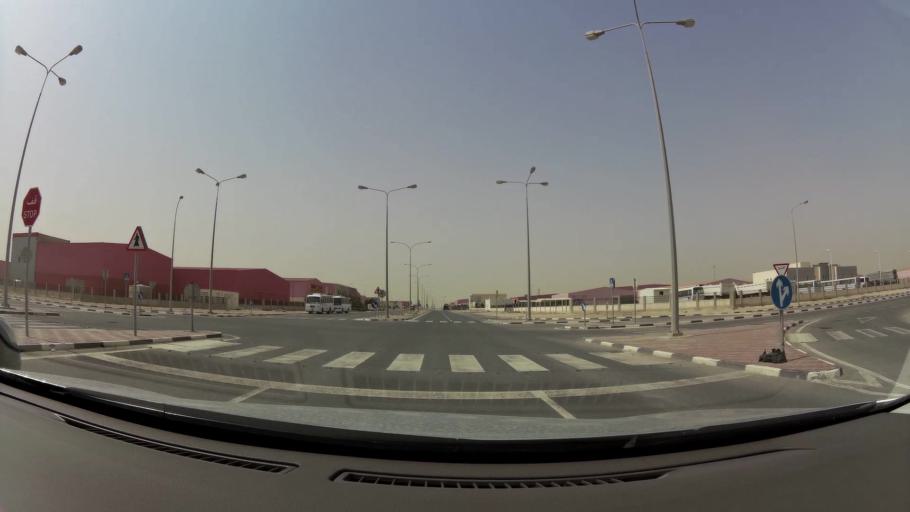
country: QA
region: Al Wakrah
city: Al Wukayr
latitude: 25.1538
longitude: 51.4056
